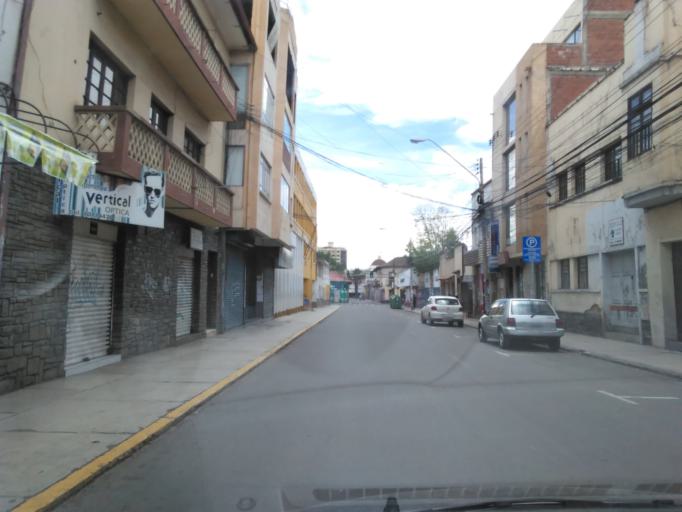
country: BO
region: Cochabamba
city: Cochabamba
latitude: -17.3897
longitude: -66.1551
